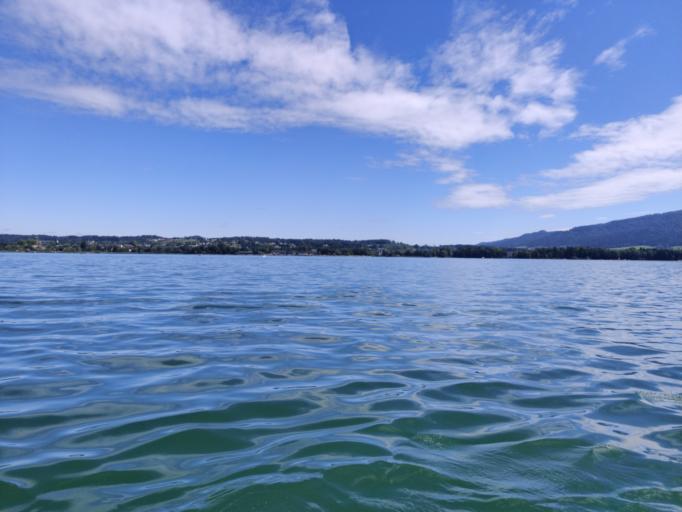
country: DE
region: Bavaria
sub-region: Swabia
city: Lindau
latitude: 47.5365
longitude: 9.7056
